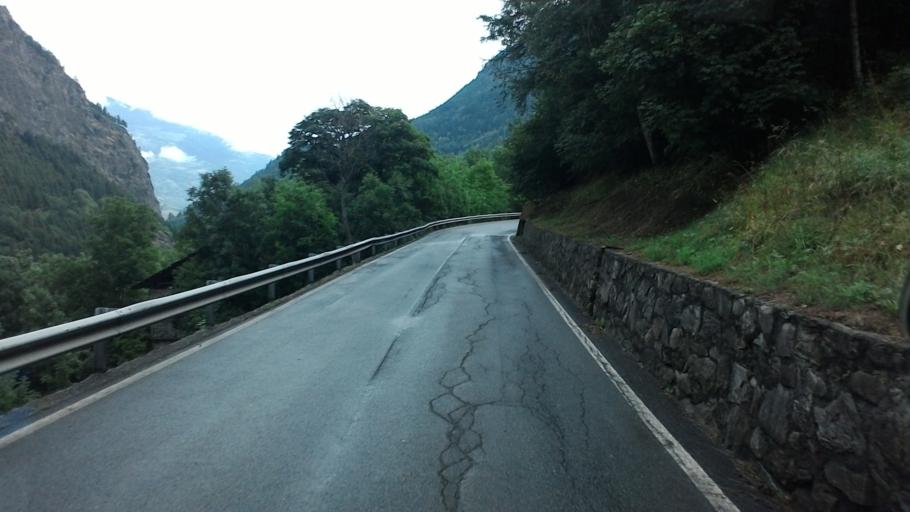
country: IT
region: Aosta Valley
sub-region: Valle d'Aosta
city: Rhemes-Saint-Georges
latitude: 45.6689
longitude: 7.1673
